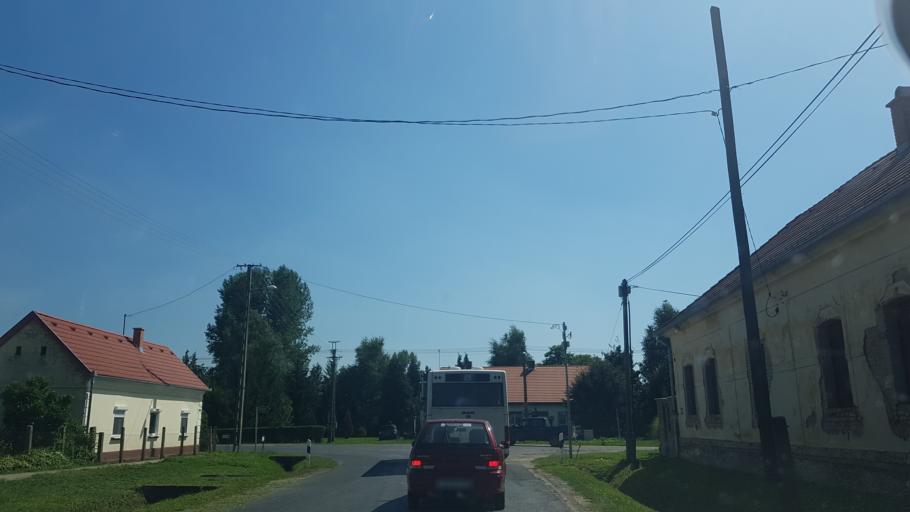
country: HU
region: Somogy
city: Segesd
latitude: 46.2943
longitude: 17.2920
